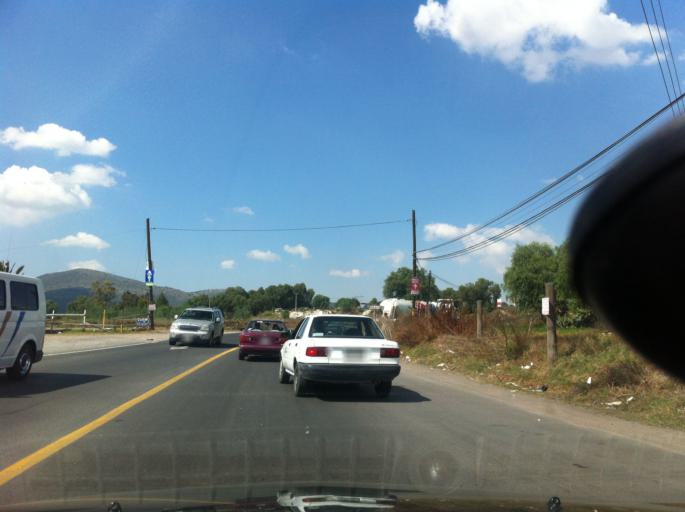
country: MX
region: Mexico
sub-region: Zumpango
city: Santa Maria de Guadalupe
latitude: 19.8158
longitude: -99.1136
